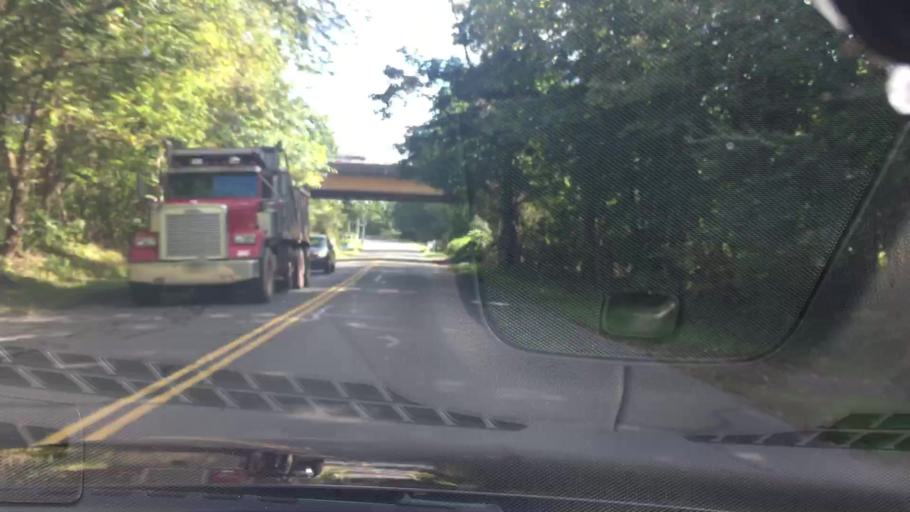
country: US
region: Connecticut
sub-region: Hartford County
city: Plainville
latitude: 41.6768
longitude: -72.8800
